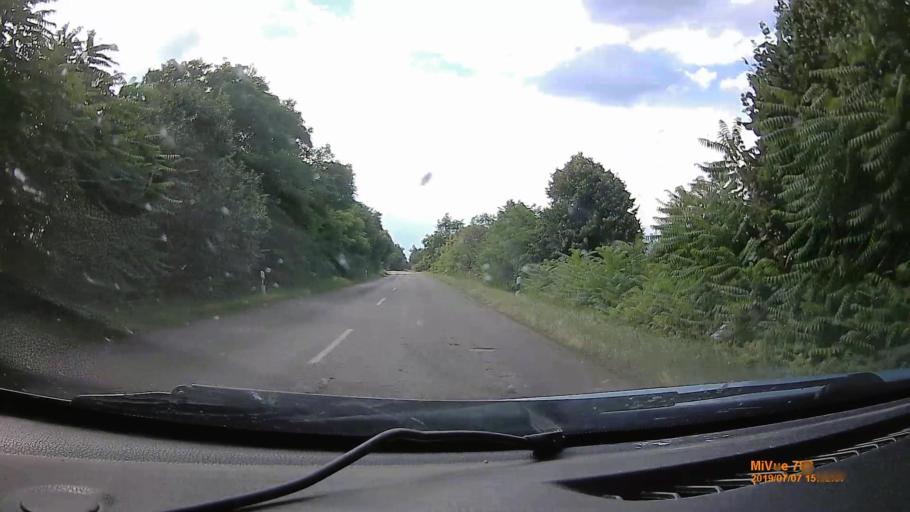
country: HU
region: Pest
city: Szentlorinckata
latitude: 47.5387
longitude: 19.8282
